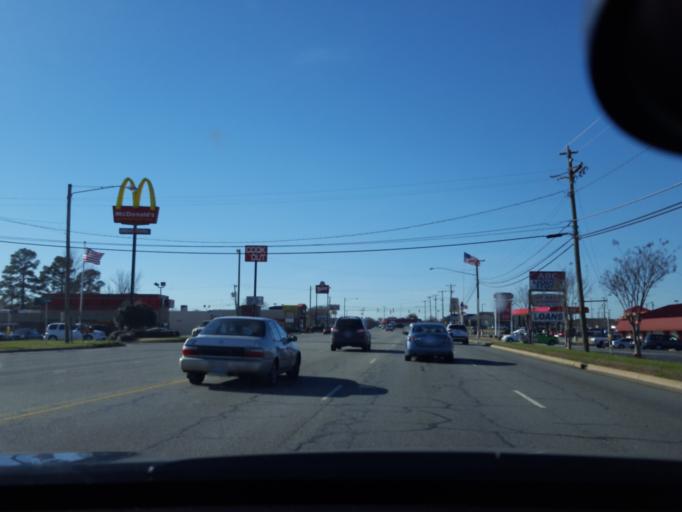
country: US
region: North Carolina
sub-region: Halifax County
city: Roanoke Rapids
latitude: 36.4332
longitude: -77.6356
